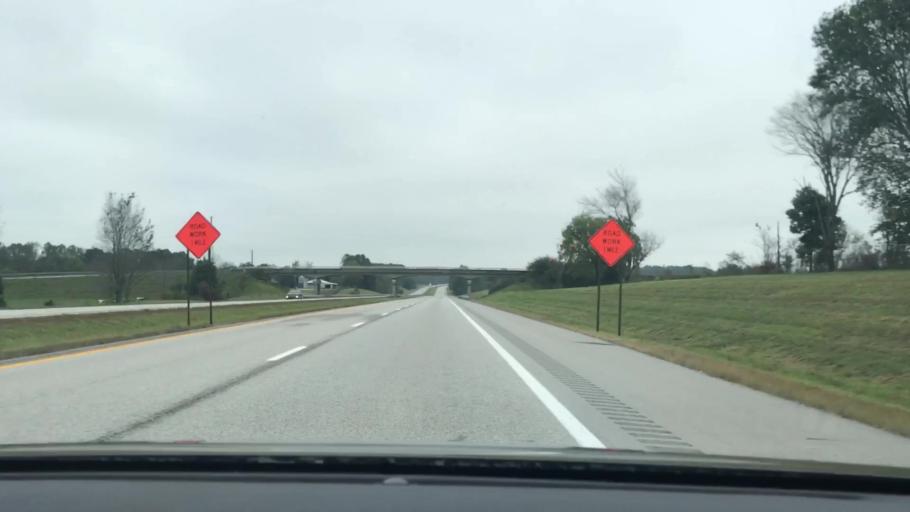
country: US
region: Kentucky
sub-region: Russell County
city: Russell Springs
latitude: 37.0773
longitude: -84.9545
